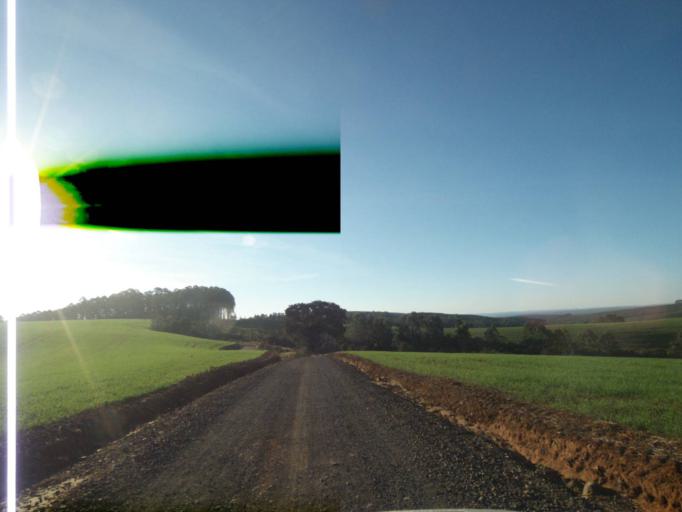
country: BR
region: Parana
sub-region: Telemaco Borba
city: Telemaco Borba
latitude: -24.4638
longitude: -50.5968
